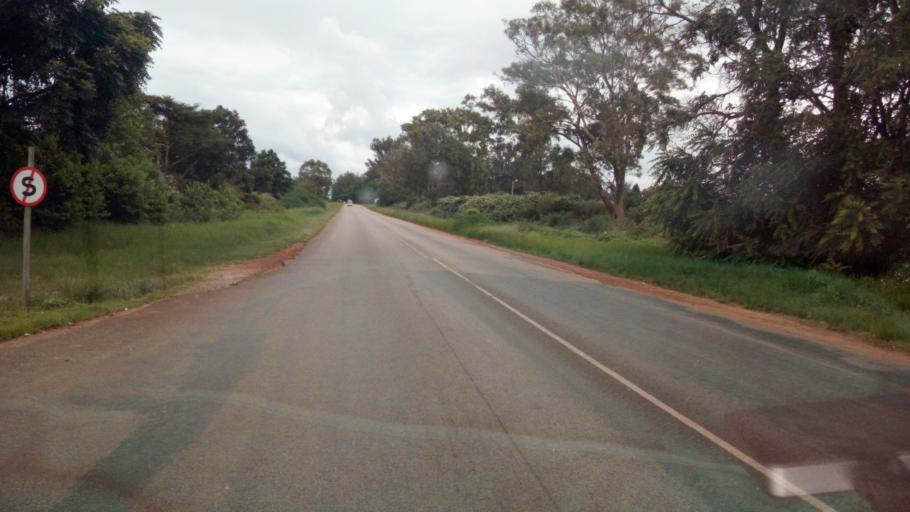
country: ZW
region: Harare
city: Harare
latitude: -17.6904
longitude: 31.0075
